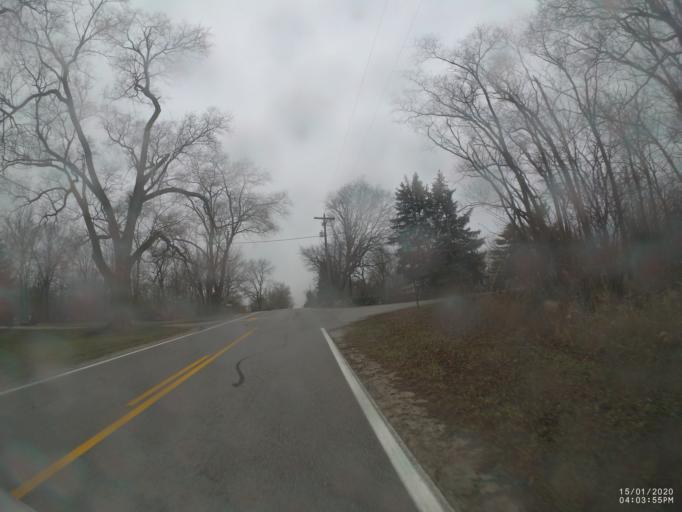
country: US
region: Ohio
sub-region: Sandusky County
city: Woodville
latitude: 41.4138
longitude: -83.3867
